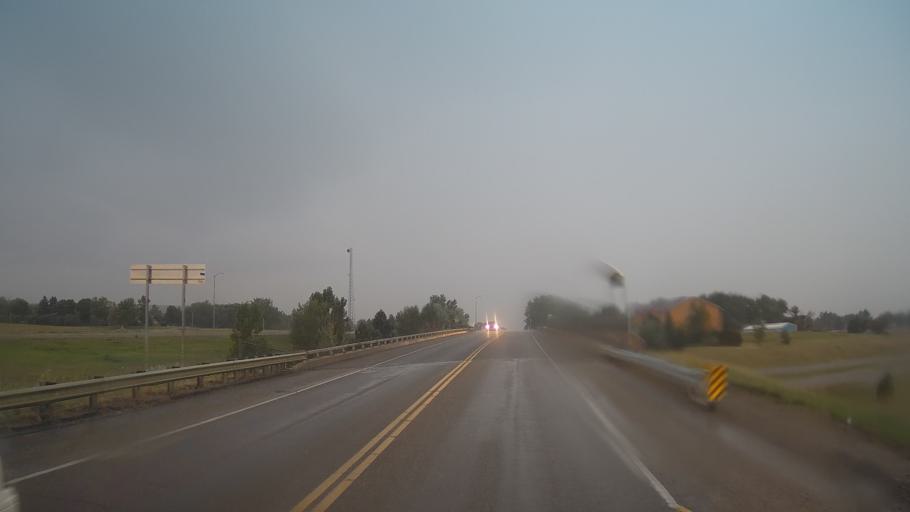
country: US
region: Montana
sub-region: Dawson County
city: Glendive
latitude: 47.1246
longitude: -104.6940
